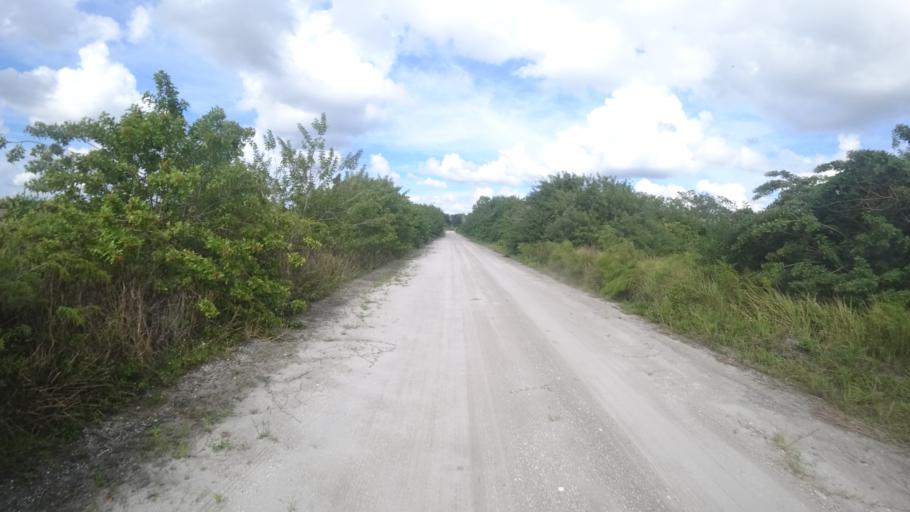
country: US
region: Florida
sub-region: Hillsborough County
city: Wimauma
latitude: 27.5922
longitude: -82.2670
